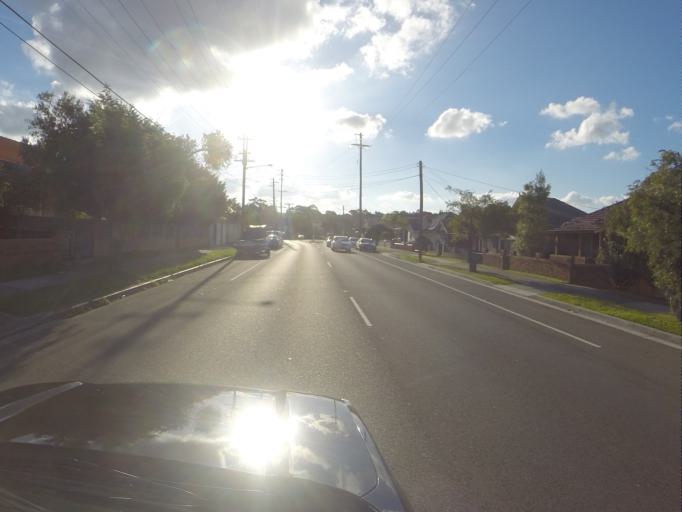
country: AU
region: New South Wales
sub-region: Kogarah
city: Kogarah Bay
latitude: -33.9758
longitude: 151.1198
